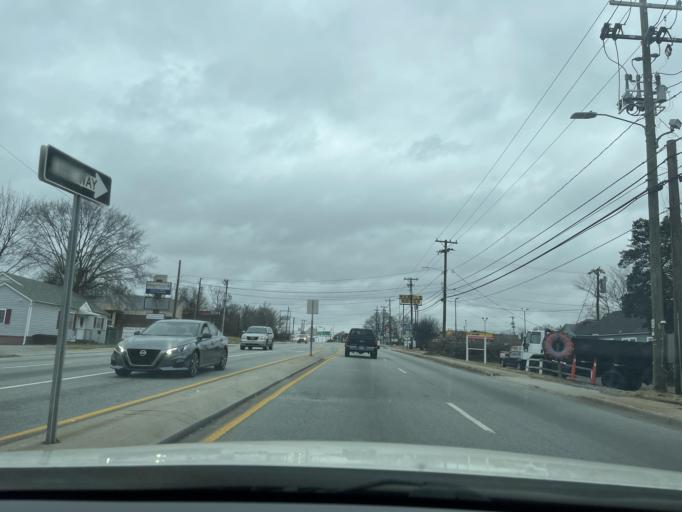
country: US
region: North Carolina
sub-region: Guilford County
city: Greensboro
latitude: 36.0306
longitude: -79.8014
